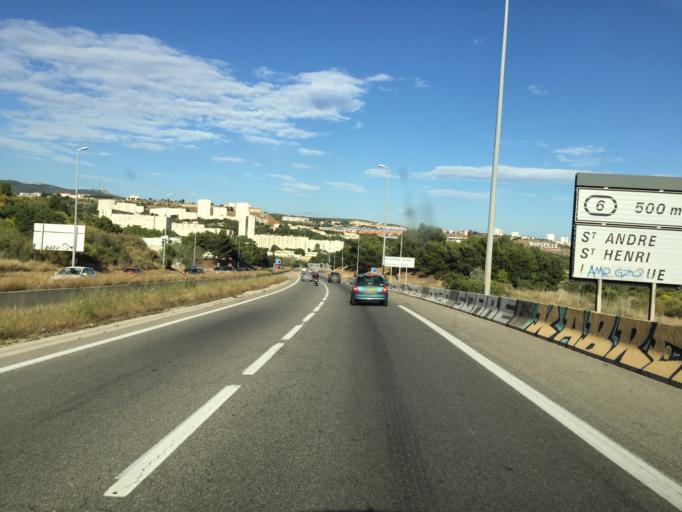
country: FR
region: Provence-Alpes-Cote d'Azur
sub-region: Departement des Bouches-du-Rhone
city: Marseille 16
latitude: 43.3662
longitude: 5.3312
